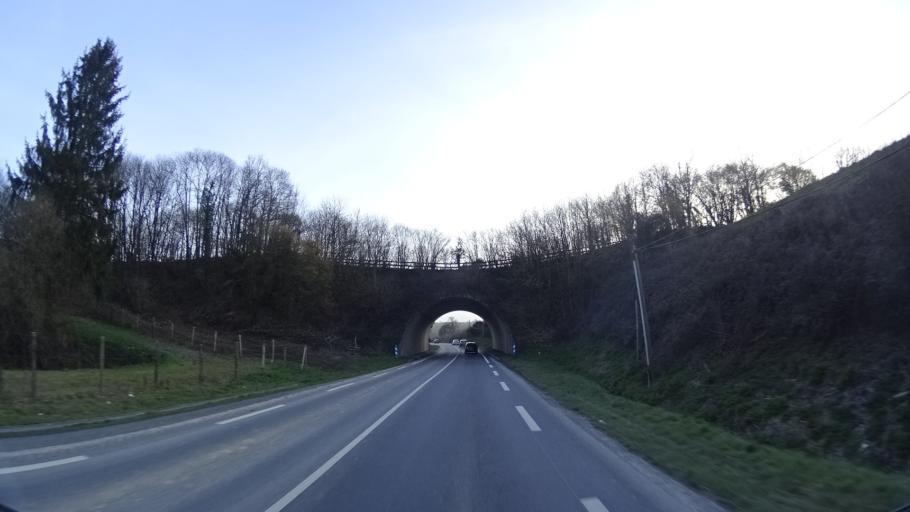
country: FR
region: Brittany
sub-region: Departement d'Ille-et-Vilaine
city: Vitre
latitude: 48.1005
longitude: -1.2240
